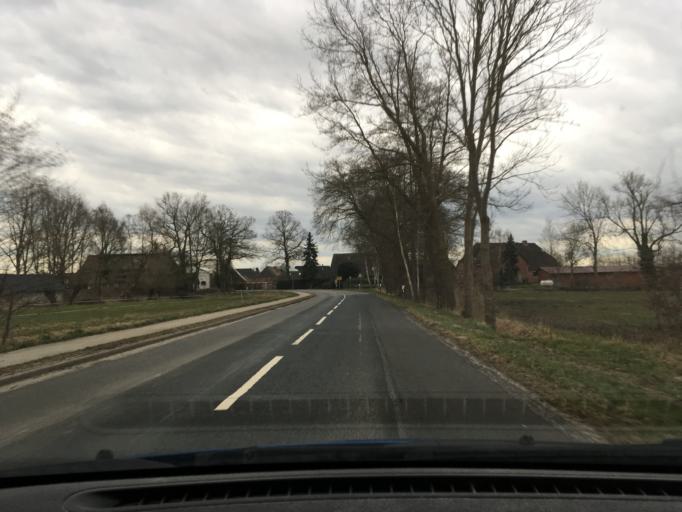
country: DE
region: Lower Saxony
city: Handorf
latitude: 53.3499
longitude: 10.3420
